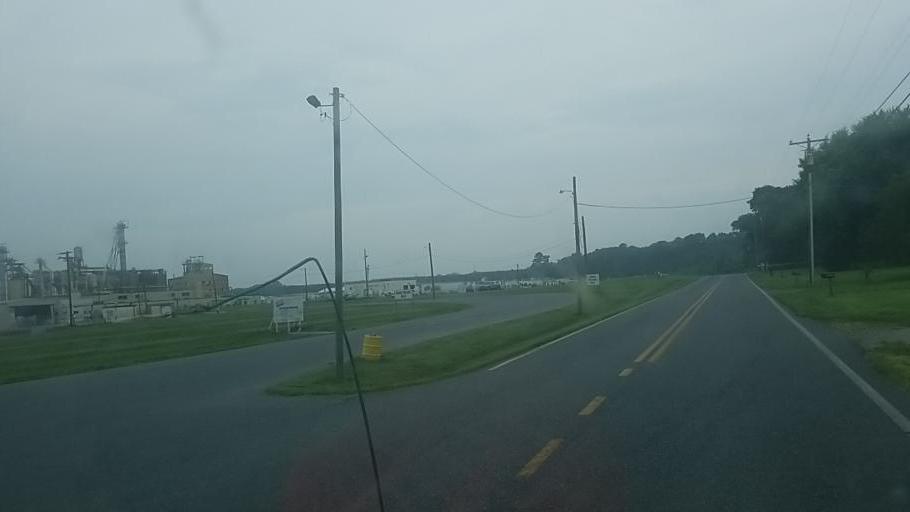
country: US
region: Maryland
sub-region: Wicomico County
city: Salisbury
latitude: 38.3819
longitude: -75.5259
